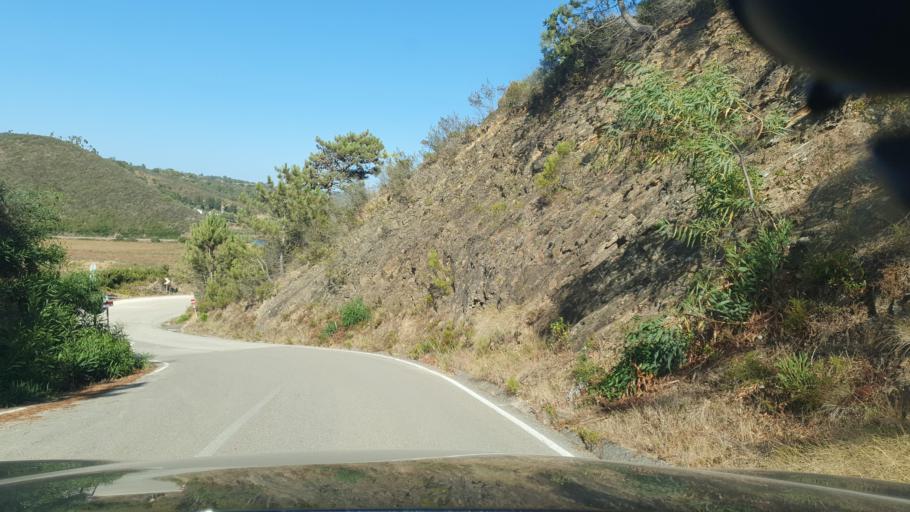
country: PT
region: Beja
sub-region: Odemira
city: Sao Teotonio
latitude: 37.4349
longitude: -8.7909
